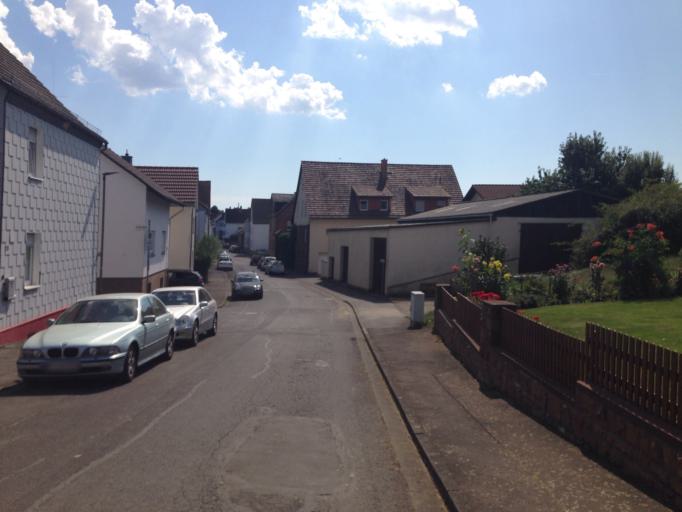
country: DE
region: Hesse
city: Allendorf an der Lahn
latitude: 50.5404
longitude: 8.6180
